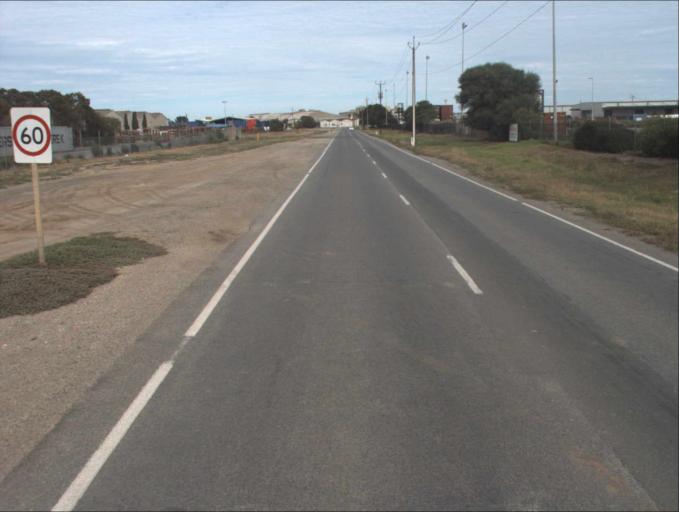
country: AU
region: South Australia
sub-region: Port Adelaide Enfield
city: Birkenhead
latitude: -34.8289
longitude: 138.5186
